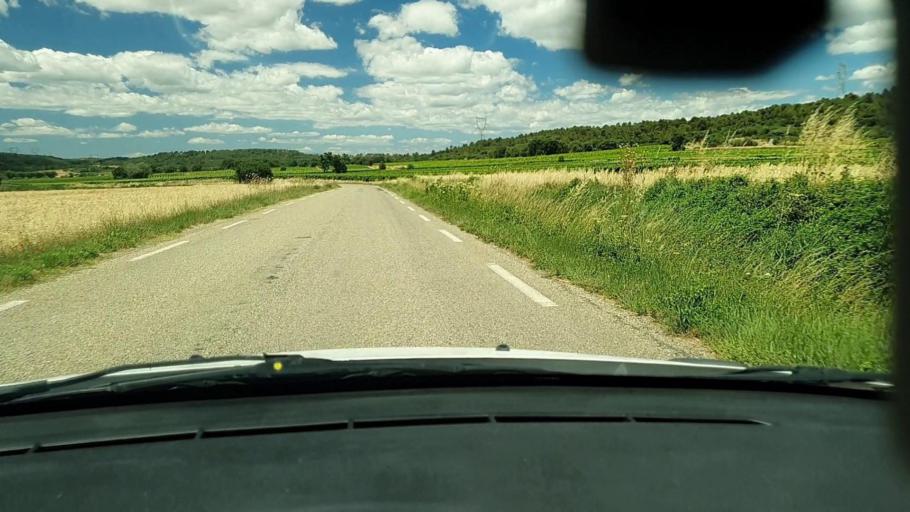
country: FR
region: Languedoc-Roussillon
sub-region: Departement du Gard
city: Blauzac
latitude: 43.9524
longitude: 4.4081
